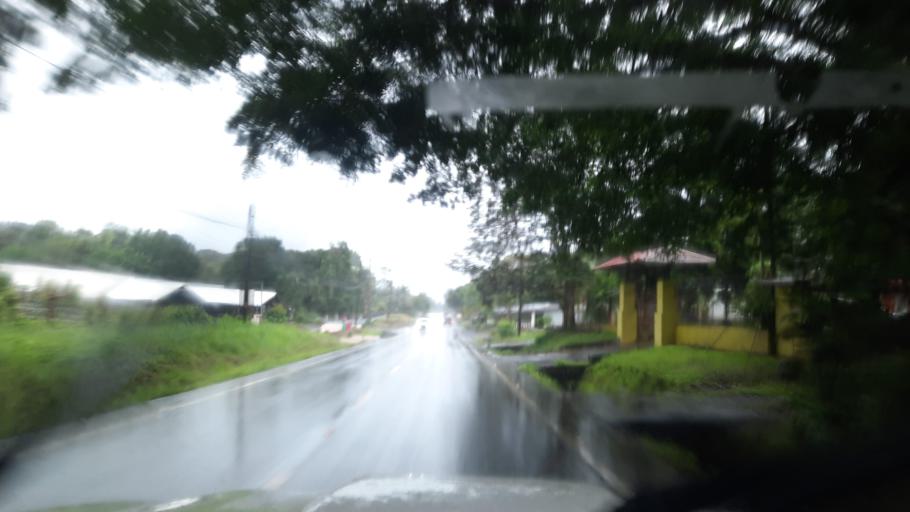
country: PA
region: Chiriqui
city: Sortova
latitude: 8.5739
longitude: -82.6348
